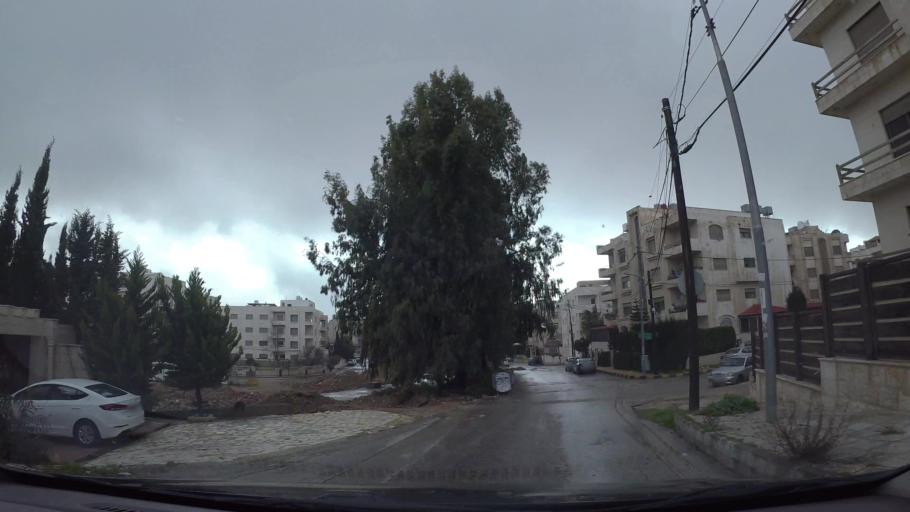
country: JO
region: Amman
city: Wadi as Sir
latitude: 31.9436
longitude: 35.8525
